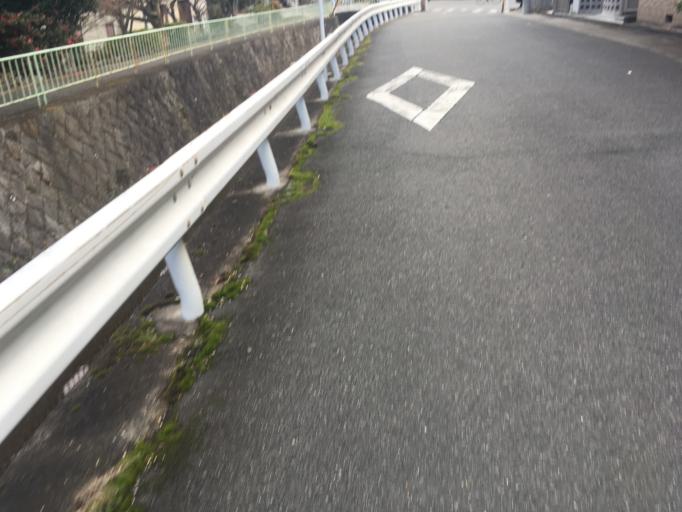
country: JP
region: Kyoto
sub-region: Kyoto-shi
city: Kamigyo-ku
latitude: 35.0371
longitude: 135.7879
